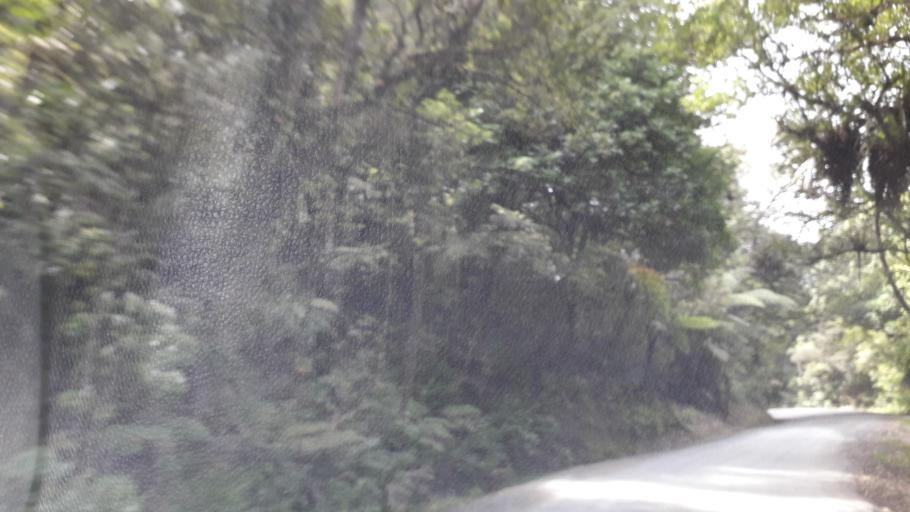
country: NZ
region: Northland
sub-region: Far North District
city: Kaitaia
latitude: -35.1706
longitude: 173.3341
